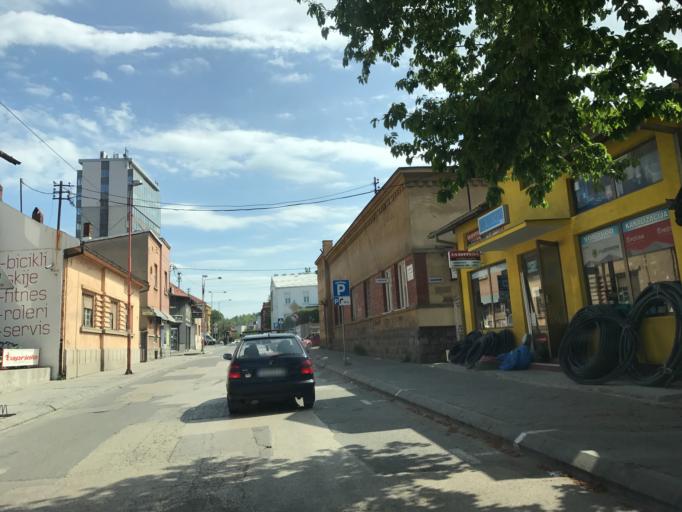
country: RS
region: Central Serbia
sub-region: Zajecarski Okrug
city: Zajecar
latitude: 43.9047
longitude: 22.2792
